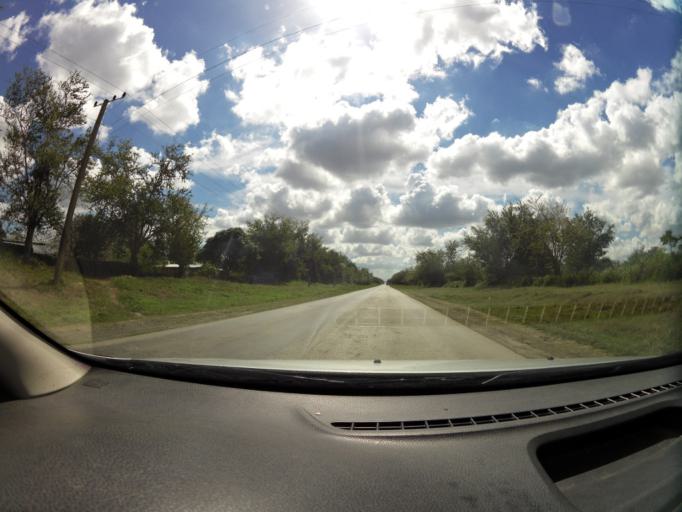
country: CU
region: Las Tunas
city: Las Tunas
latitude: 20.8539
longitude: -76.9115
